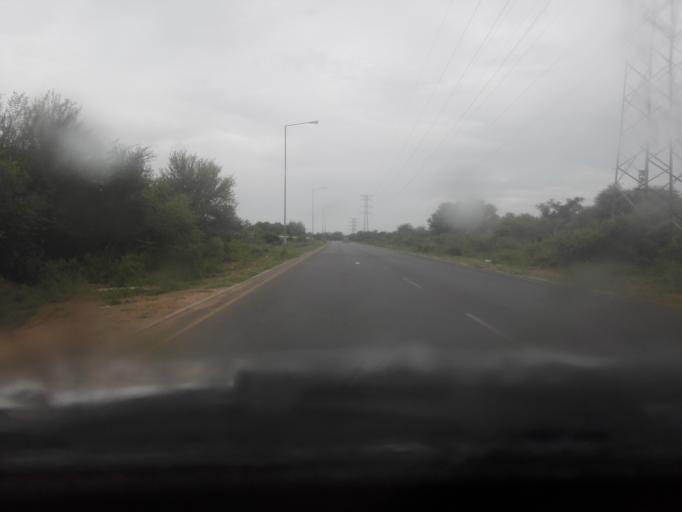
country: BW
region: South East
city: Gaborone
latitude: -24.6383
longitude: 25.8971
